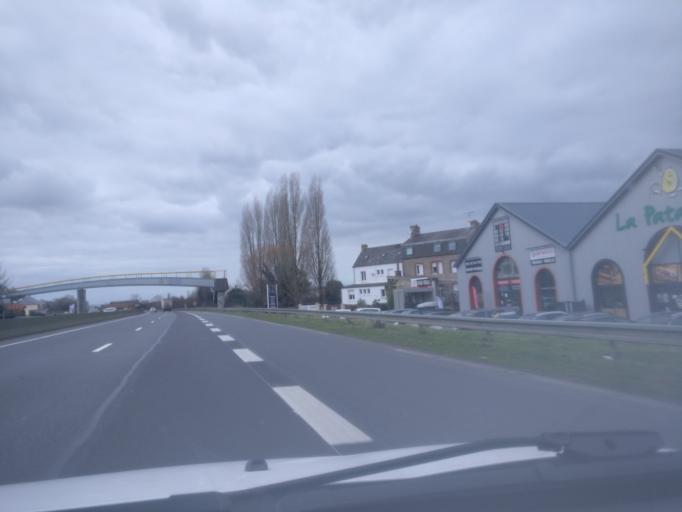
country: FR
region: Lower Normandy
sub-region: Departement de la Manche
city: Avranches
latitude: 48.6900
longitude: -1.3686
